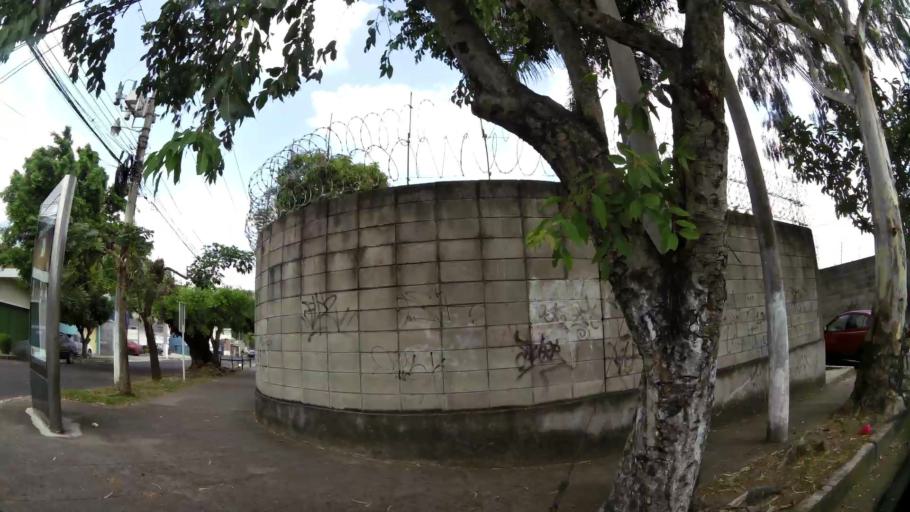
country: SV
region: San Salvador
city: Mejicanos
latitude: 13.7072
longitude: -89.2341
